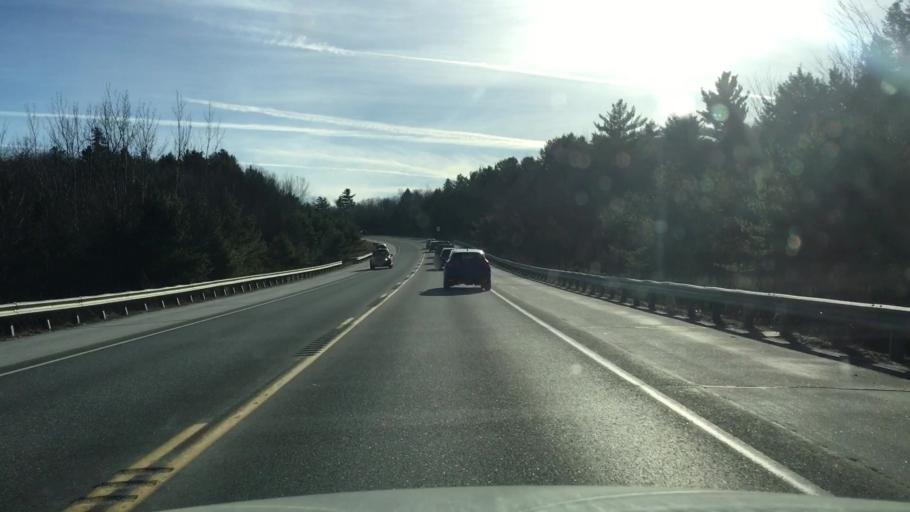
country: US
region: Maine
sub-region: Hancock County
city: Dedham
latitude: 44.6776
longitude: -68.5785
